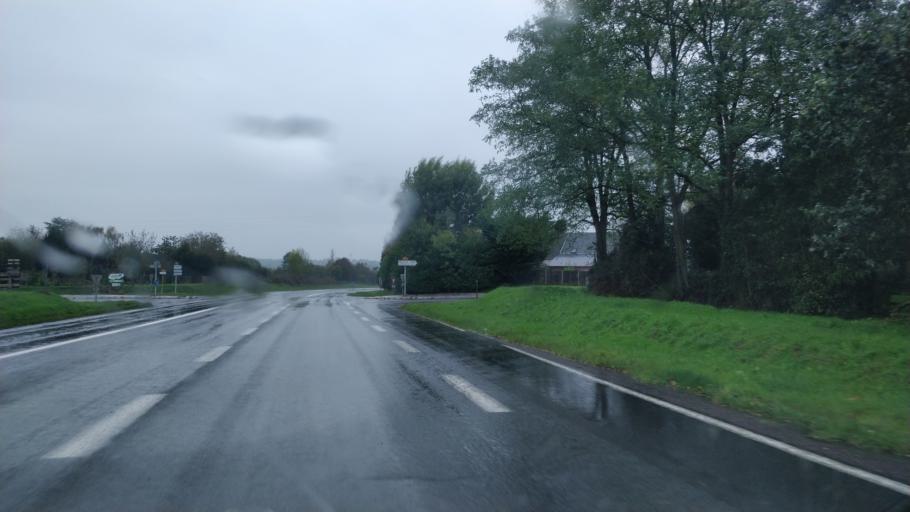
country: FR
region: Lower Normandy
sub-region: Departement de la Manche
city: Saint-Planchers
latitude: 48.8624
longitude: -1.5394
